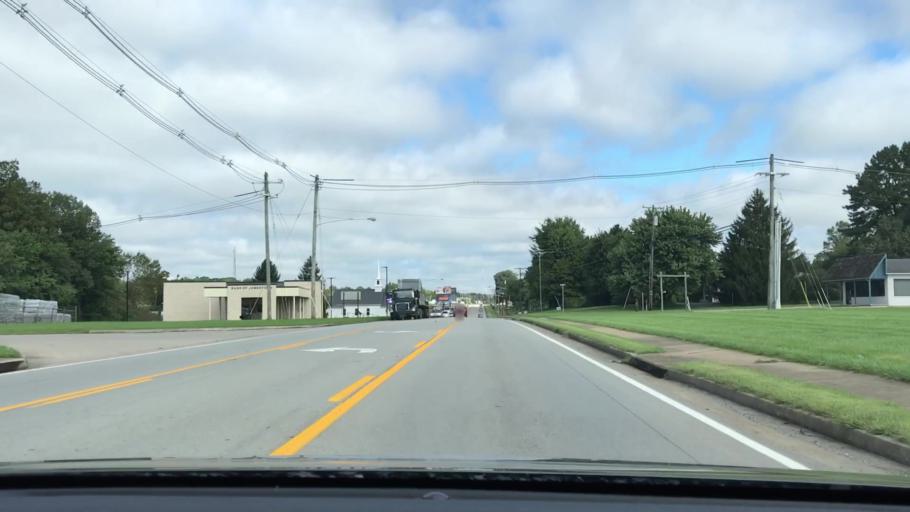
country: US
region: Kentucky
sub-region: Russell County
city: Jamestown
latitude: 37.0133
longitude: -85.0756
